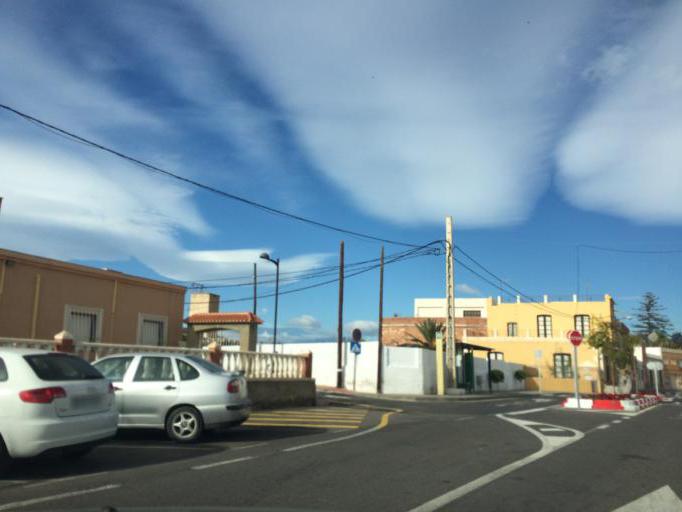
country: ES
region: Andalusia
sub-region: Provincia de Almeria
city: Rioja
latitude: 36.9431
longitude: -2.4622
